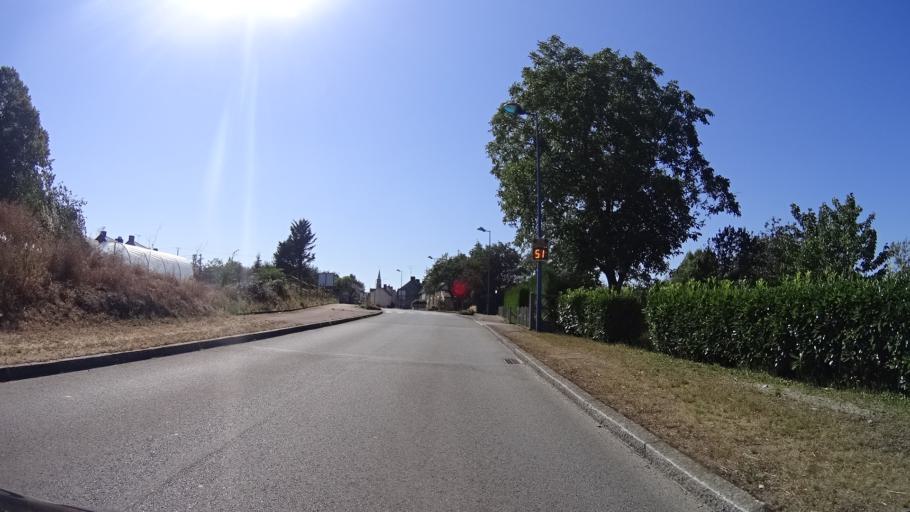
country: FR
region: Brittany
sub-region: Departement du Morbihan
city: Saint-Dolay
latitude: 47.5441
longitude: -2.1487
